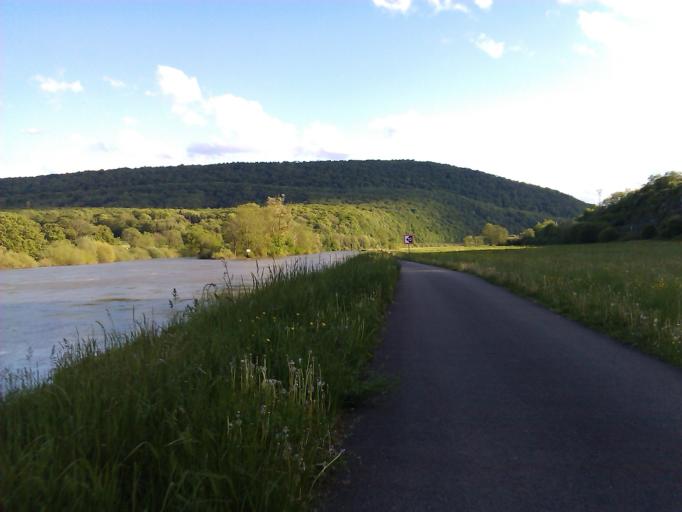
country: FR
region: Franche-Comte
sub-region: Departement du Doubs
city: Clerval
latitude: 47.4104
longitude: 6.5114
